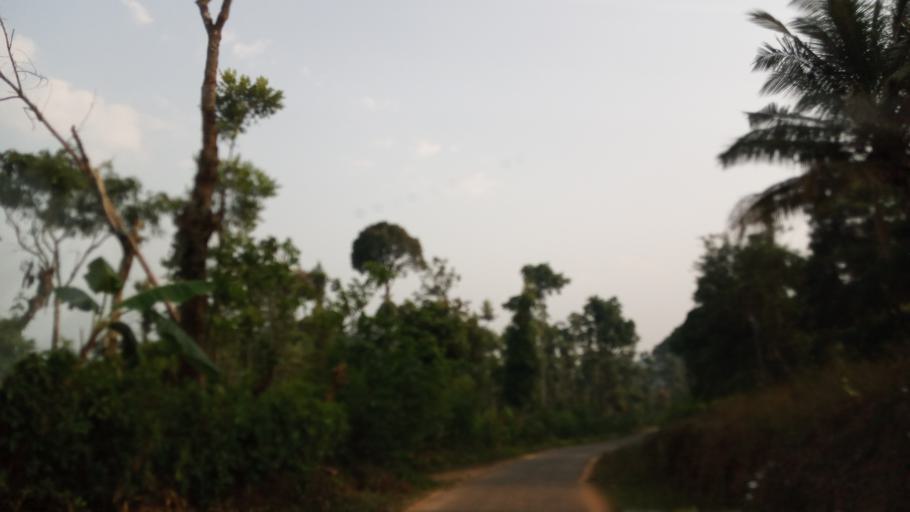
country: IN
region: Karnataka
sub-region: Chikmagalur
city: Mudigere
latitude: 13.0247
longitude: 75.6319
